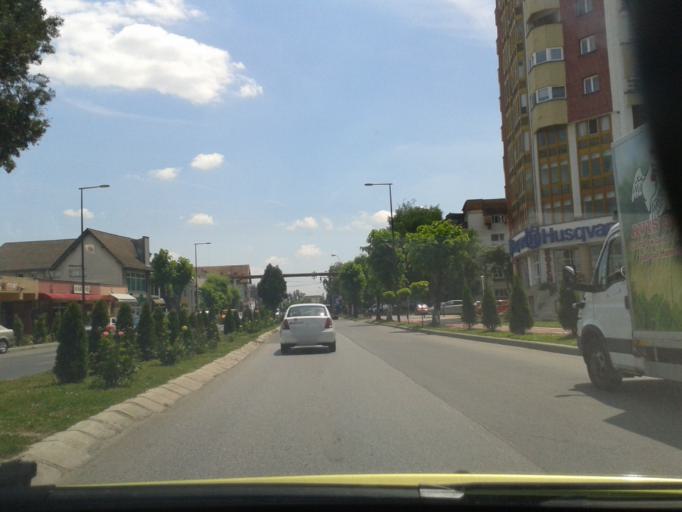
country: RO
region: Hunedoara
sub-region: Municipiul Deva
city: Deva
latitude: 45.8830
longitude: 22.9091
